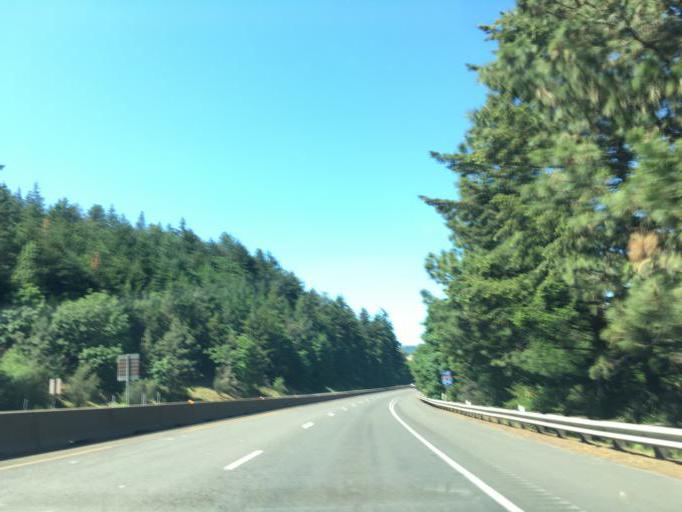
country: US
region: Oregon
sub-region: Wasco County
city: Chenoweth
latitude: 45.6954
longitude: -121.3459
